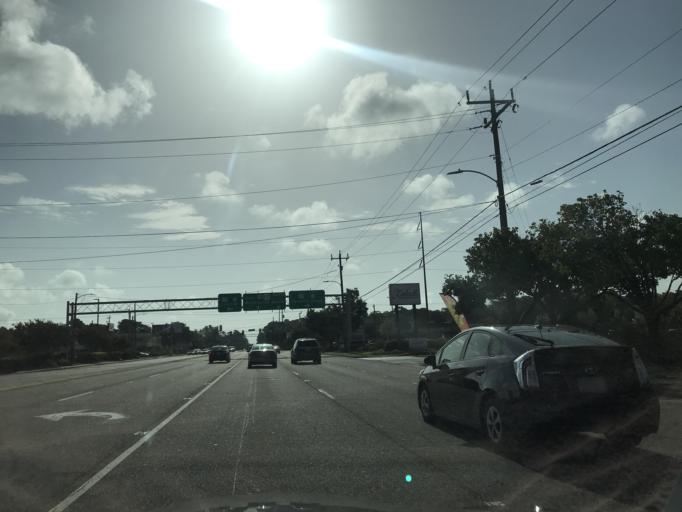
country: US
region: North Carolina
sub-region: New Hanover County
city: Seagate
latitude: 34.2105
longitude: -77.8884
